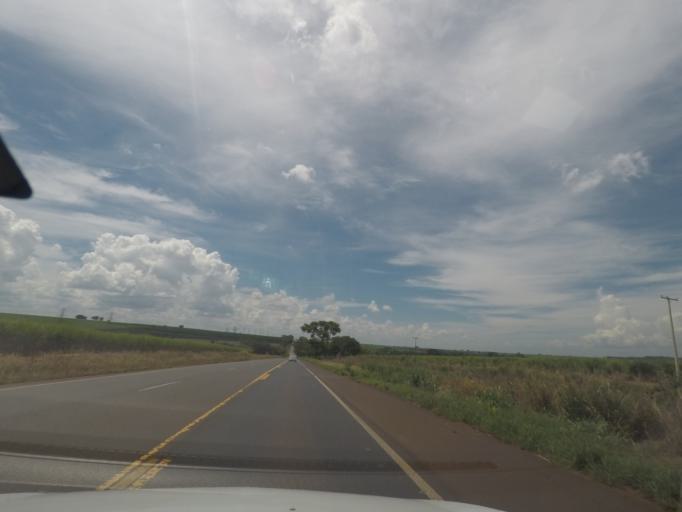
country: BR
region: Sao Paulo
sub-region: Barretos
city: Barretos
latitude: -20.2656
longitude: -48.6740
